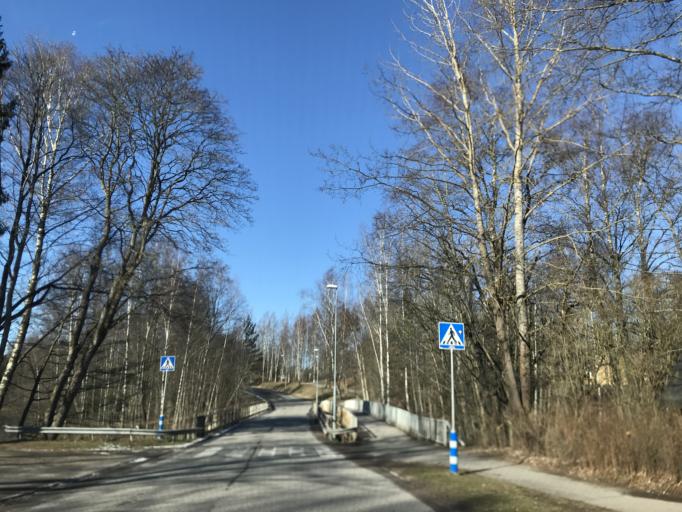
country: FI
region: Uusimaa
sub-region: Raaseporin
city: Karis
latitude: 60.0767
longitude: 23.6799
